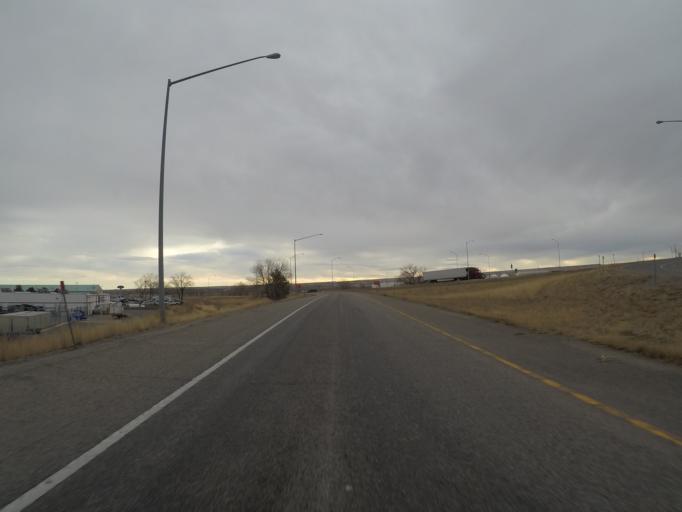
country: US
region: Montana
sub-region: Yellowstone County
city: Laurel
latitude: 45.6643
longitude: -108.7681
